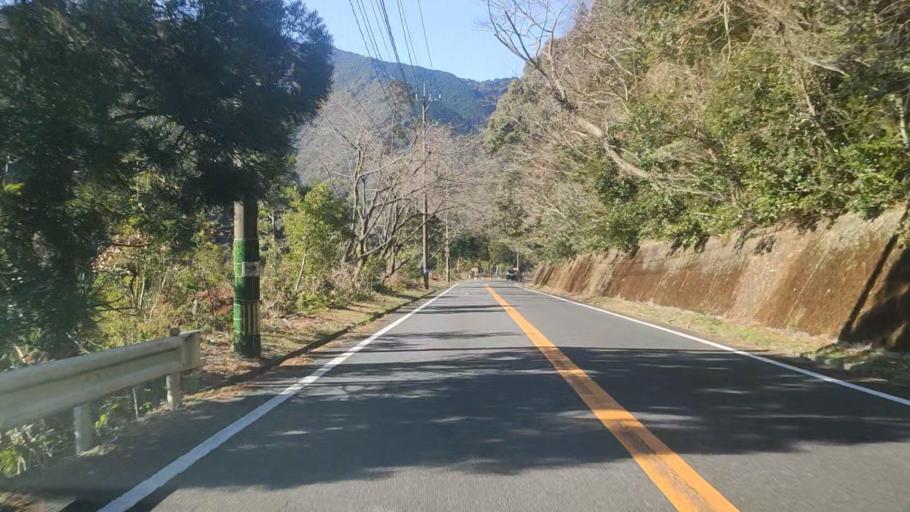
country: JP
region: Oita
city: Saiki
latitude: 32.8954
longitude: 131.9403
